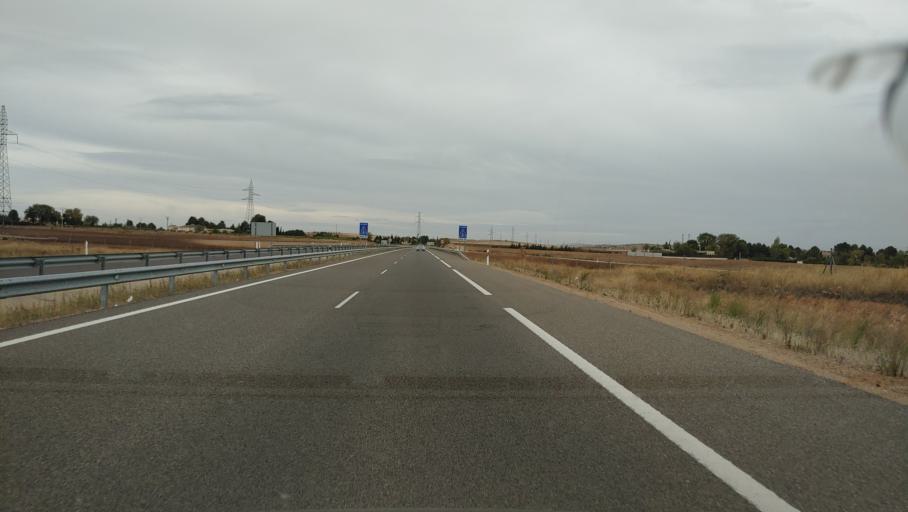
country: ES
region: Castille-La Mancha
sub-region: Provincia de Ciudad Real
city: Miguelturra
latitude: 38.9484
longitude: -3.9089
